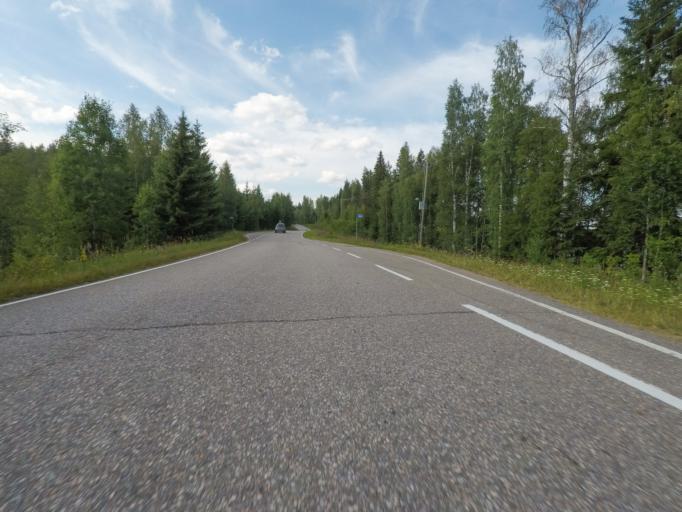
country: FI
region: Southern Savonia
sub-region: Savonlinna
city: Sulkava
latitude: 61.7318
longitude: 28.2106
